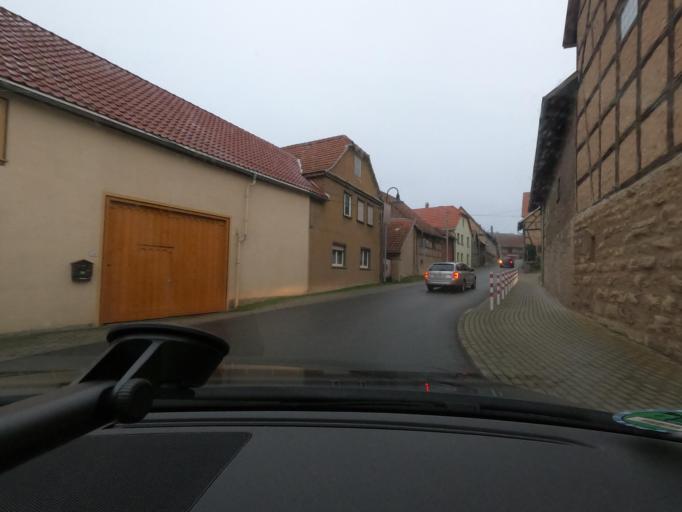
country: DE
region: Thuringia
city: Behringen
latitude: 50.7863
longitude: 10.9942
